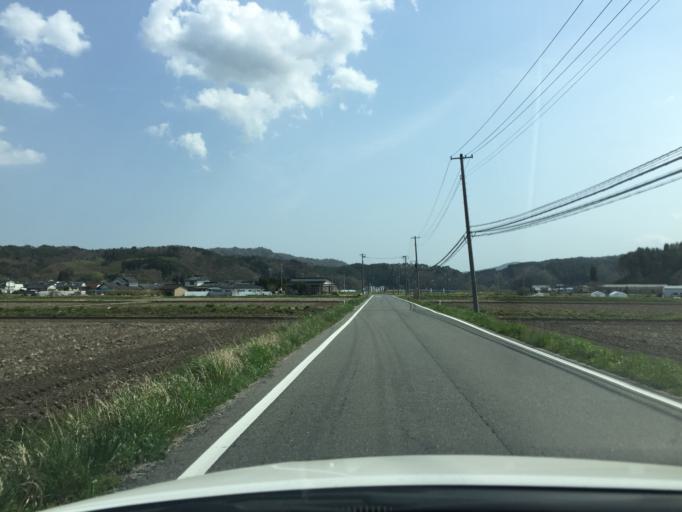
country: JP
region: Fukushima
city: Namie
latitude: 37.3214
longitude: 140.8354
